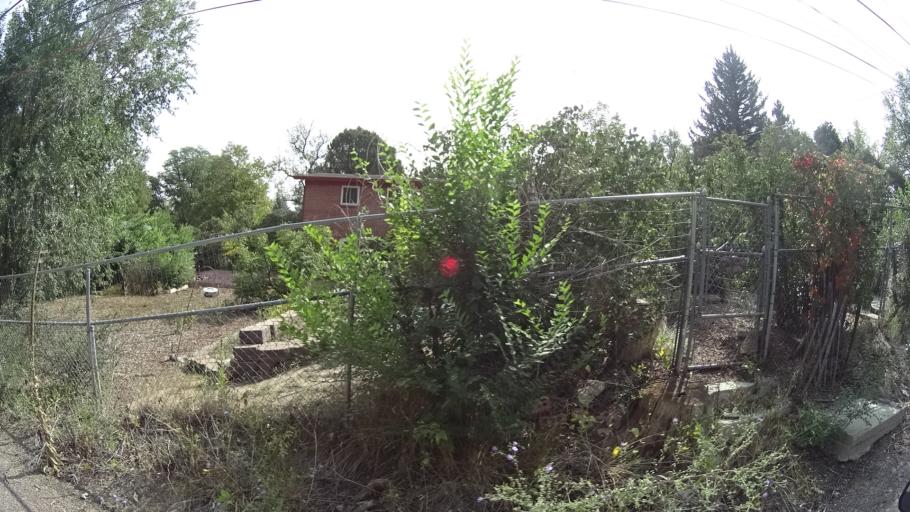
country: US
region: Colorado
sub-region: El Paso County
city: Colorado Springs
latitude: 38.8524
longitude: -104.7907
